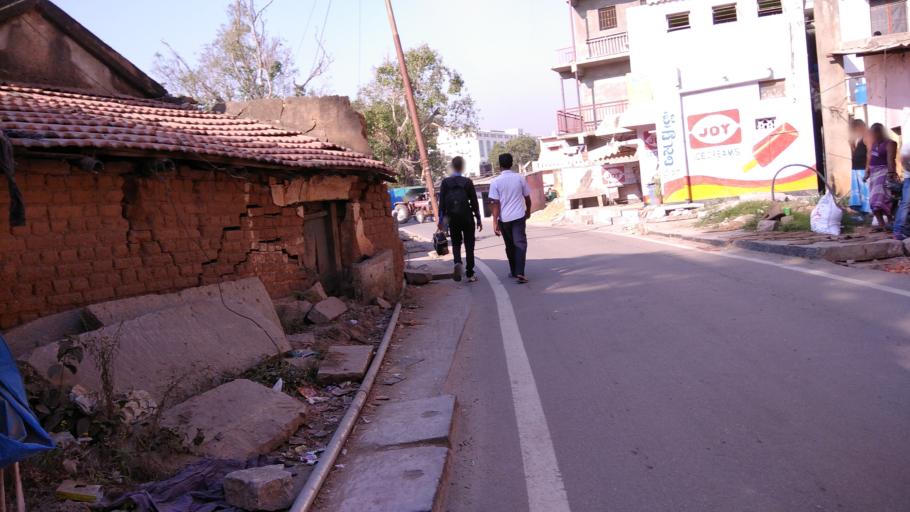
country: IN
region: Karnataka
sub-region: Bangalore Rural
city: Hoskote
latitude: 12.9781
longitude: 77.7340
